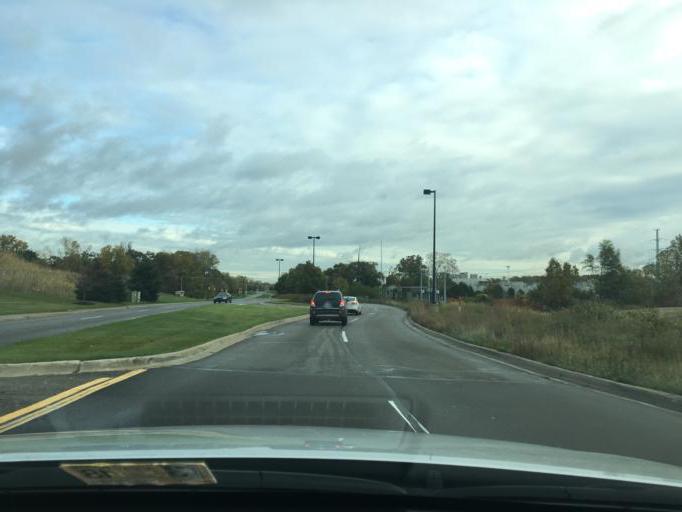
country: US
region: Michigan
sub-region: Wayne County
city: Melvindale
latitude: 42.2857
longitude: -83.2033
